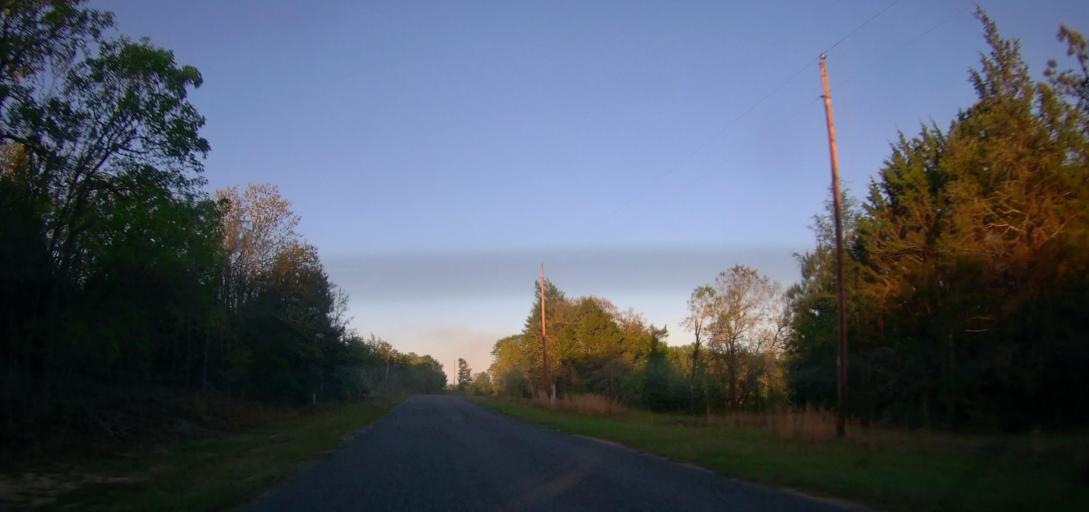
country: US
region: Georgia
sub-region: Talbot County
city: Talbotton
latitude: 32.5376
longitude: -84.5857
